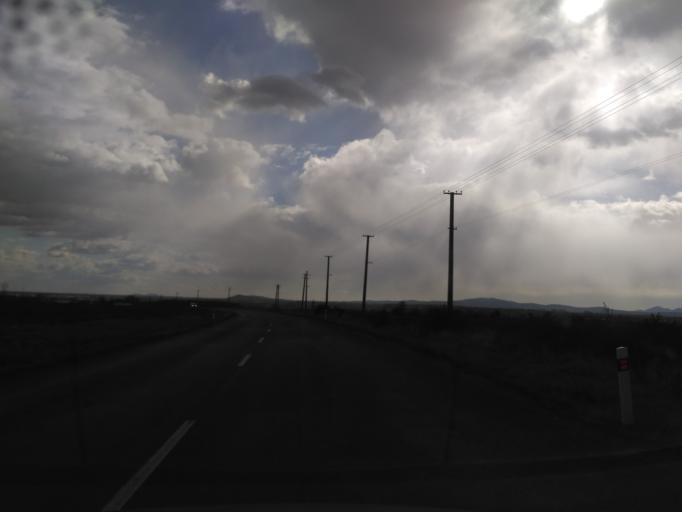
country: SK
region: Kosicky
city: Secovce
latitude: 48.6607
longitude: 21.6644
